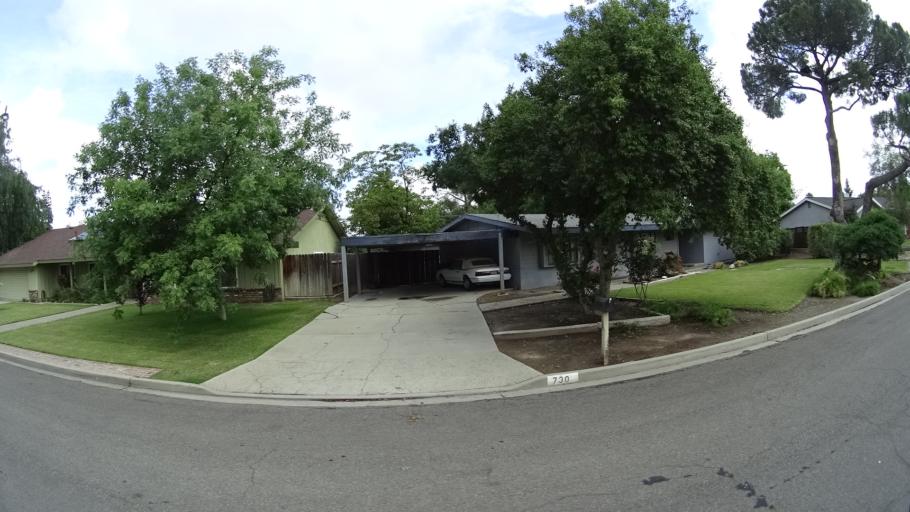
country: US
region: California
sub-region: Kings County
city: Hanford
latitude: 36.3495
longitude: -119.6564
